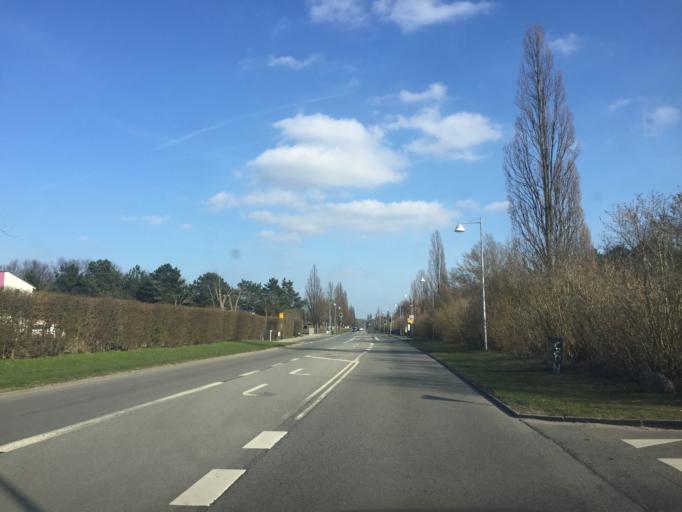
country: DK
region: Capital Region
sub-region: Albertslund Kommune
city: Albertslund
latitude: 55.6751
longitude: 12.3600
